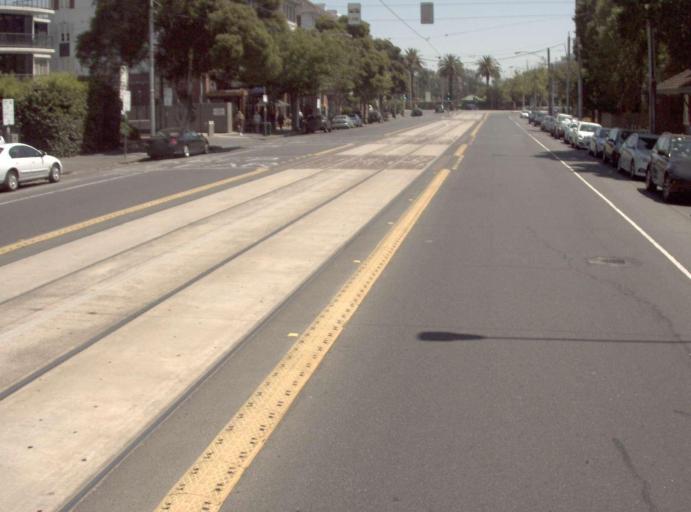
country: AU
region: Victoria
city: Windsor
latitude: -37.8451
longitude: 144.9810
